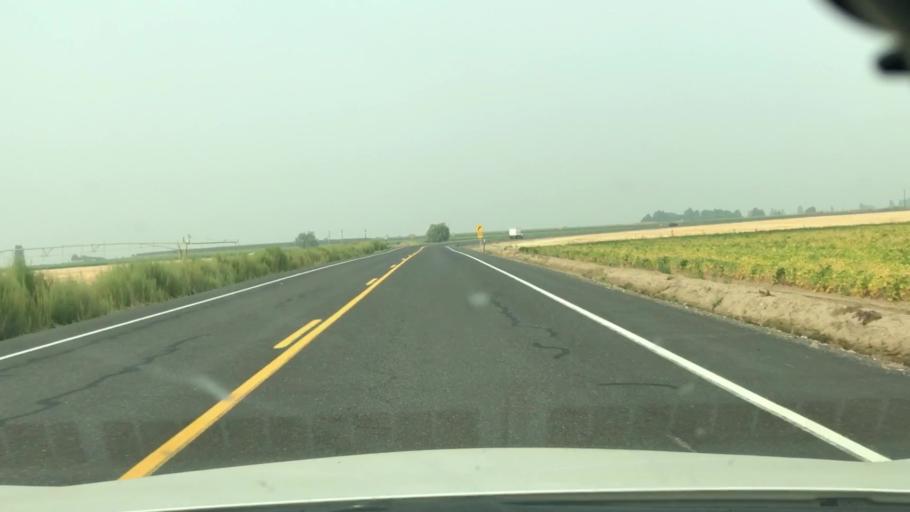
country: US
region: Washington
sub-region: Grant County
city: Quincy
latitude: 47.1636
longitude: -119.9339
